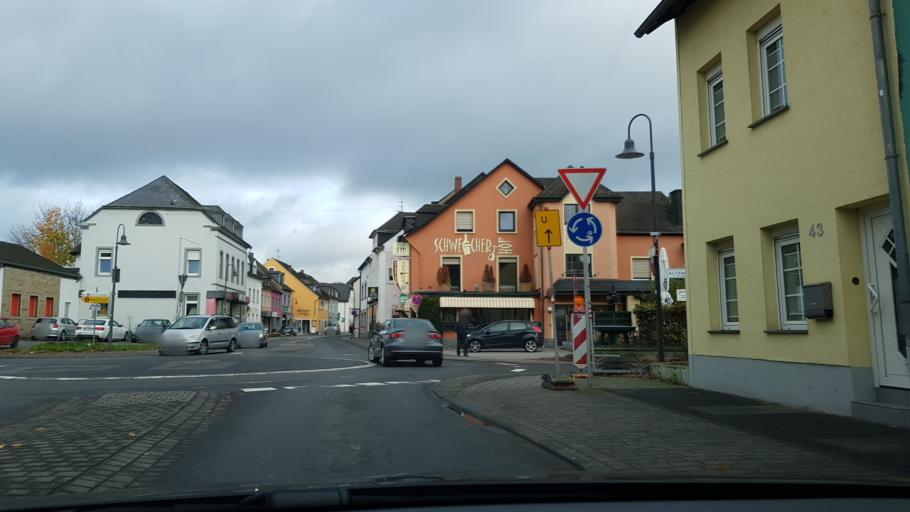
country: DE
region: Rheinland-Pfalz
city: Schweich
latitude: 49.8195
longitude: 6.7527
